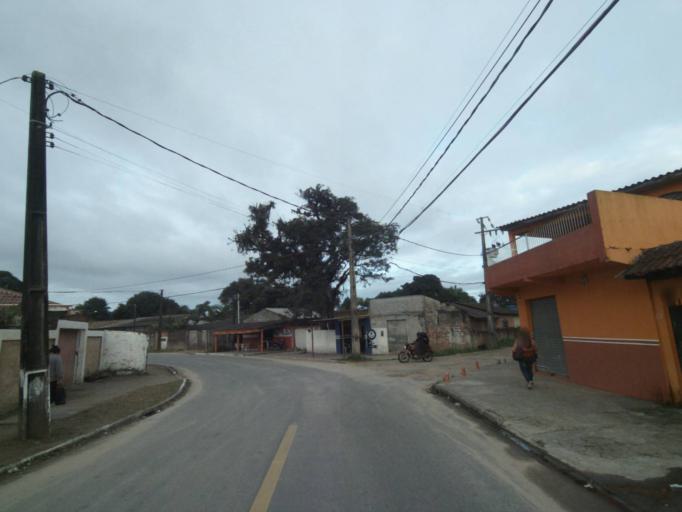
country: BR
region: Parana
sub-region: Paranagua
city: Paranagua
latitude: -25.5339
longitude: -48.5469
